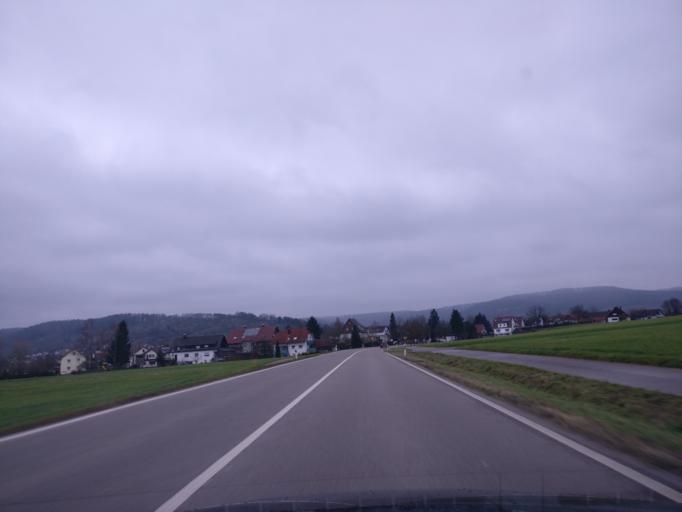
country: DE
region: Baden-Wuerttemberg
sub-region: Regierungsbezirk Stuttgart
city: Rudersberg
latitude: 48.8675
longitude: 9.5315
